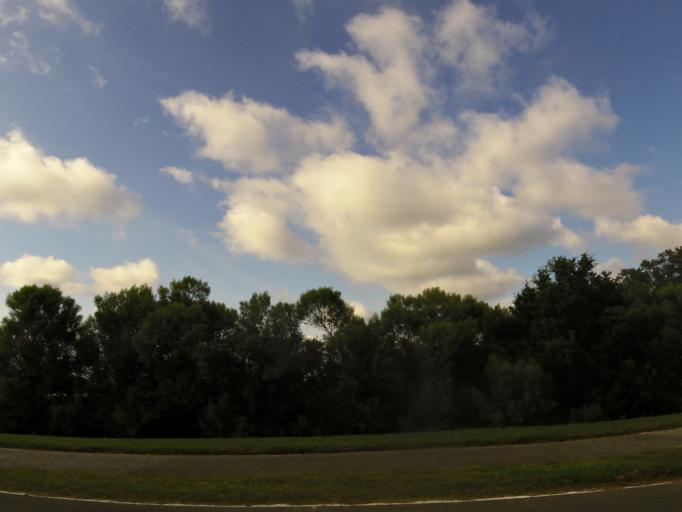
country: US
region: Georgia
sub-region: Glynn County
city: Saint Simons Island
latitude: 31.1798
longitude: -81.3556
